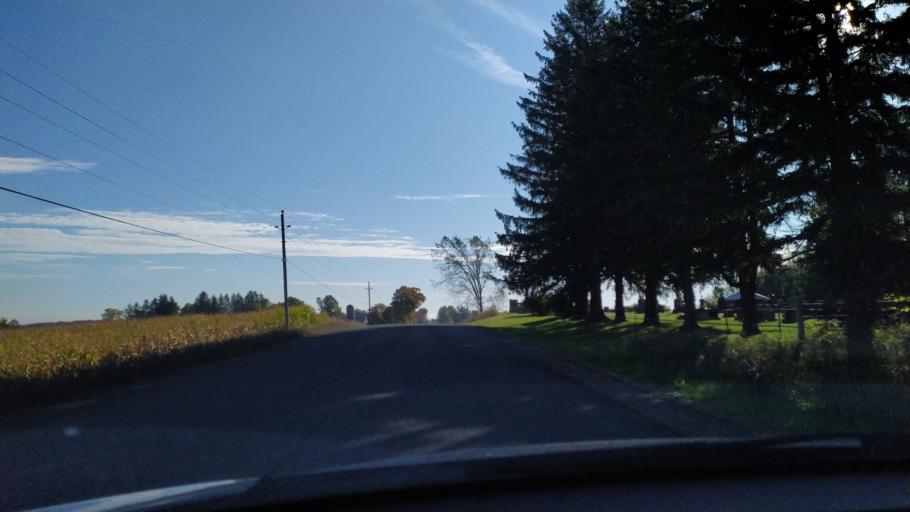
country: CA
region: Ontario
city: Stratford
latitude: 43.4619
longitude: -80.8306
